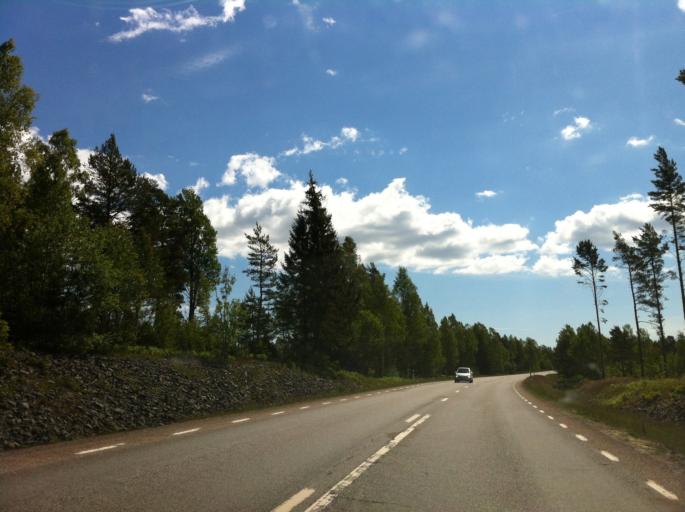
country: SE
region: Vaestra Goetaland
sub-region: Amals Kommun
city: Amal
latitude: 59.0243
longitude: 12.6781
